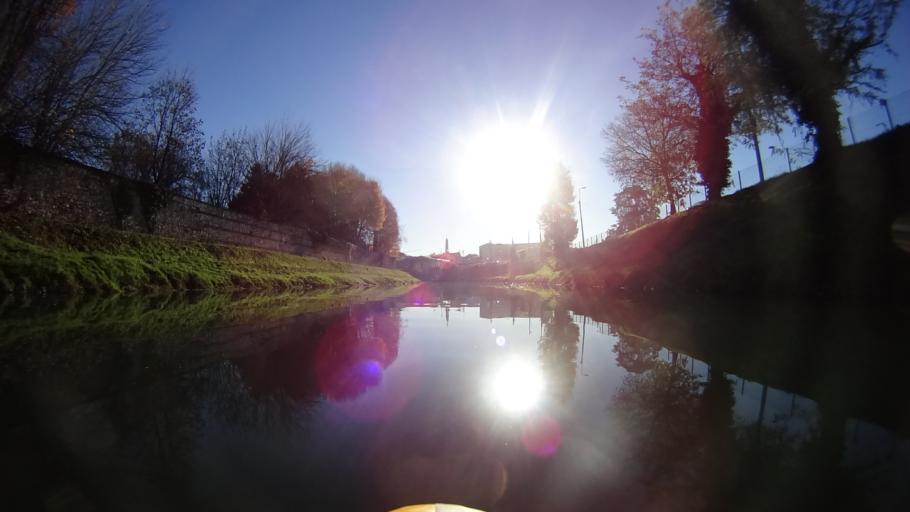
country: IT
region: Veneto
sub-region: Provincia di Vicenza
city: Vicenza
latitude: 45.5519
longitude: 11.5402
